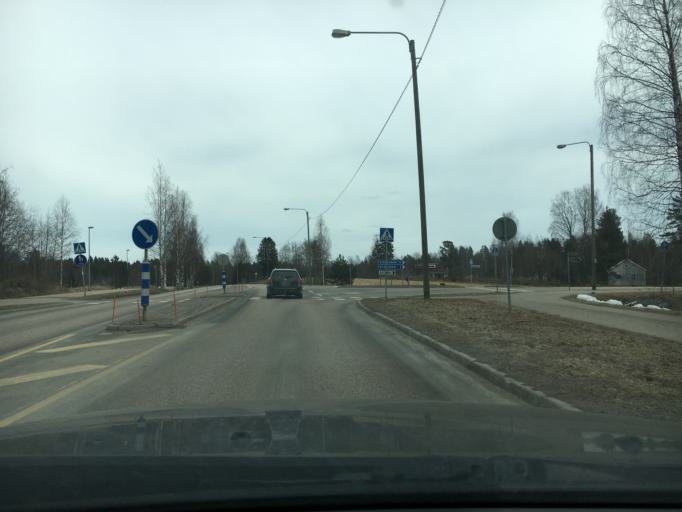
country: FI
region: Central Finland
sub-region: AEaenekoski
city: Konnevesi
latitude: 62.6289
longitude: 26.3174
